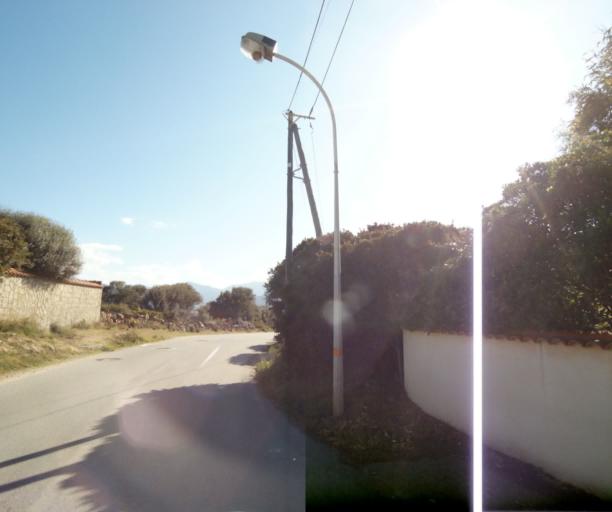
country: FR
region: Corsica
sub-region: Departement de la Corse-du-Sud
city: Propriano
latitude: 41.6726
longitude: 8.8937
